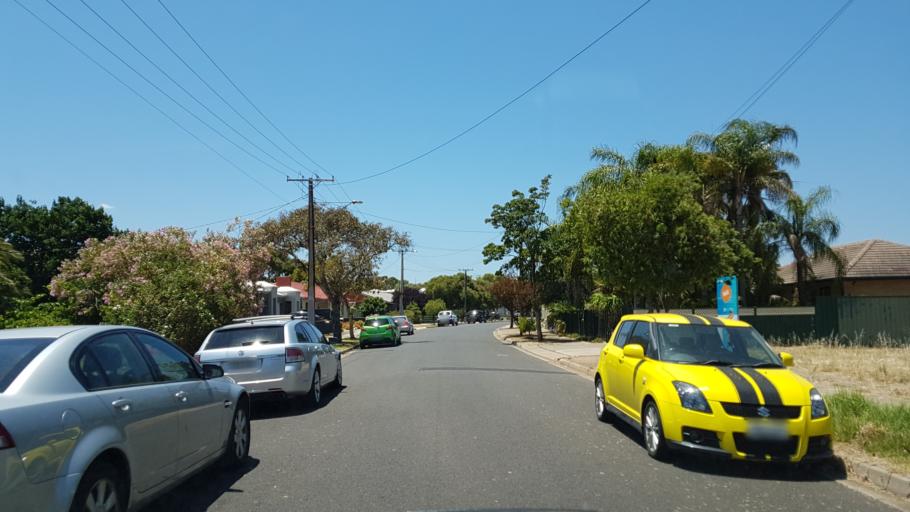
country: AU
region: South Australia
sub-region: Marion
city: Clovelly Park
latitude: -35.0037
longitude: 138.5603
